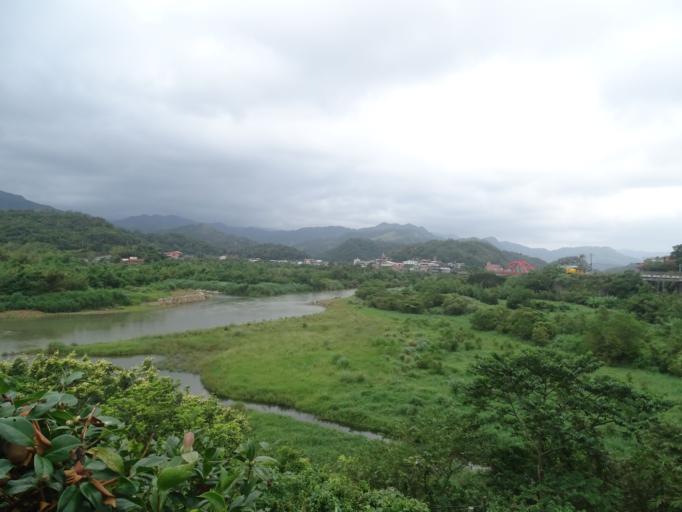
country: TW
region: Taiwan
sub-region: Keelung
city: Keelung
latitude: 25.0210
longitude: 121.9148
